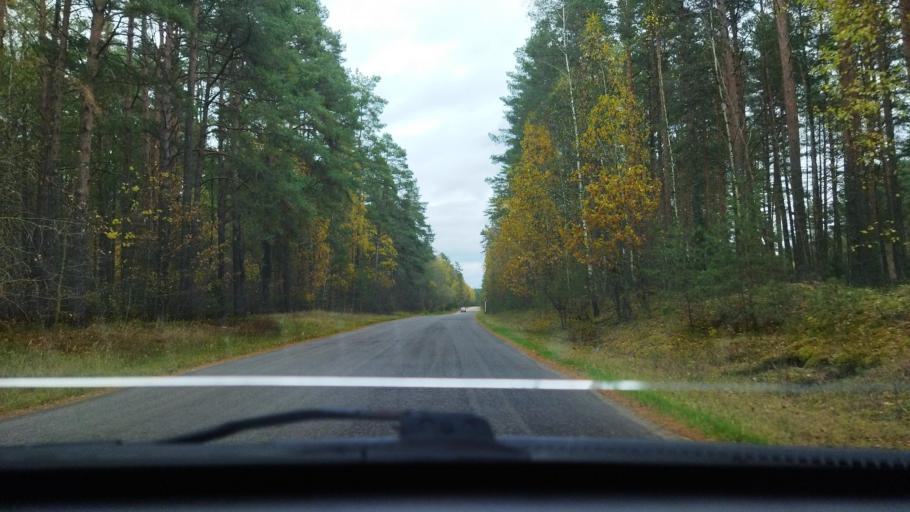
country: BY
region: Minsk
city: Svir
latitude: 54.8037
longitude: 26.2438
